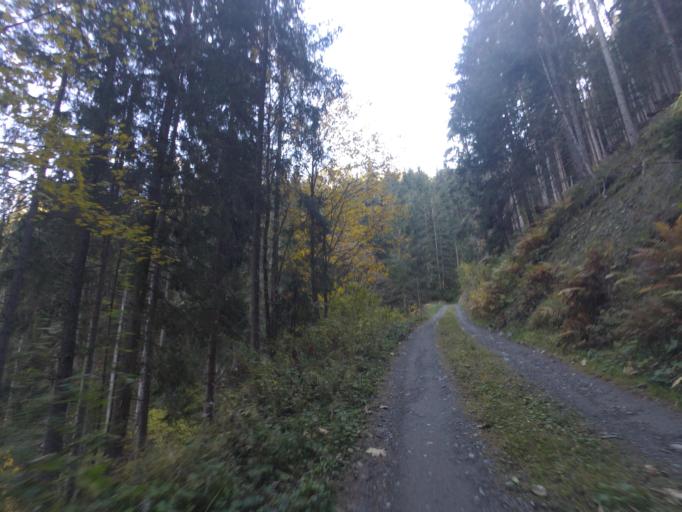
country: AT
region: Salzburg
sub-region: Politischer Bezirk Sankt Johann im Pongau
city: Sankt Johann im Pongau
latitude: 47.3269
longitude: 13.2257
